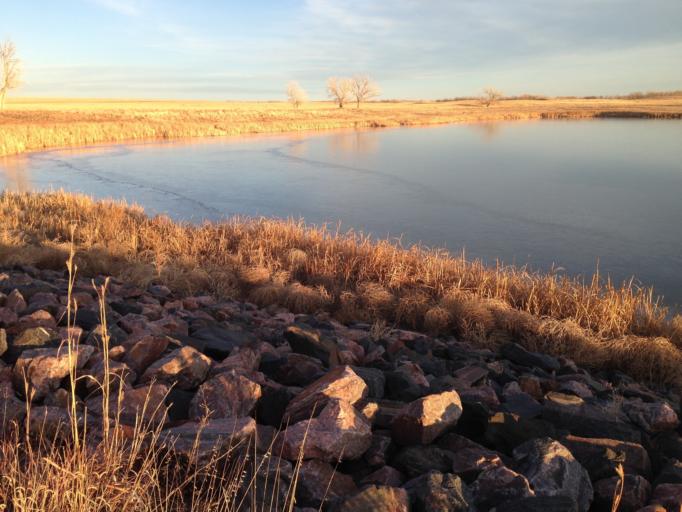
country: US
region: Colorado
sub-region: Adams County
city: Derby
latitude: 39.8214
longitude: -104.8592
